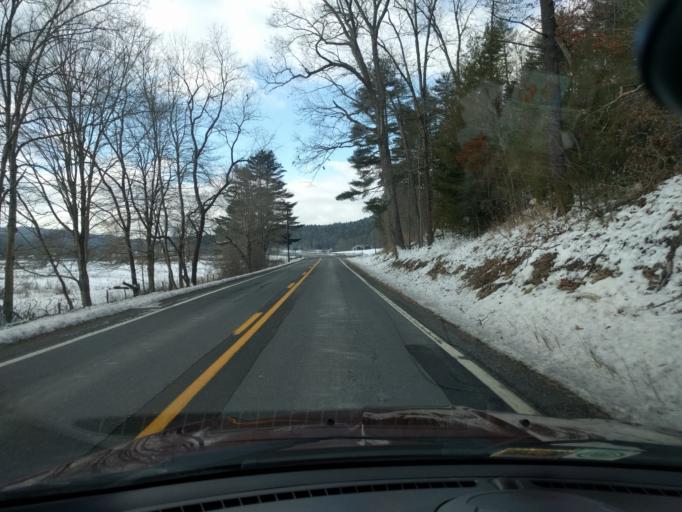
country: US
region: West Virginia
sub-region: Pocahontas County
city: Marlinton
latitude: 38.1570
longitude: -79.9807
